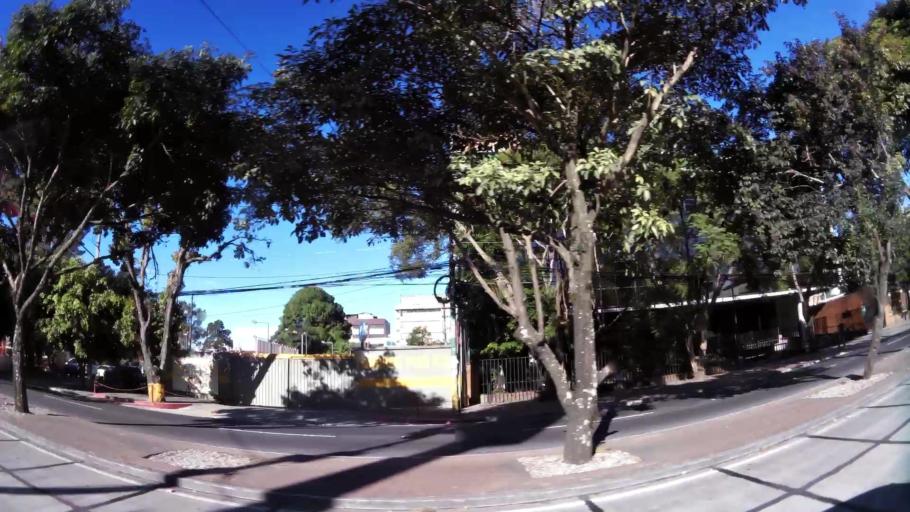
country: GT
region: Guatemala
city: Guatemala City
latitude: 14.6047
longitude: -90.5182
